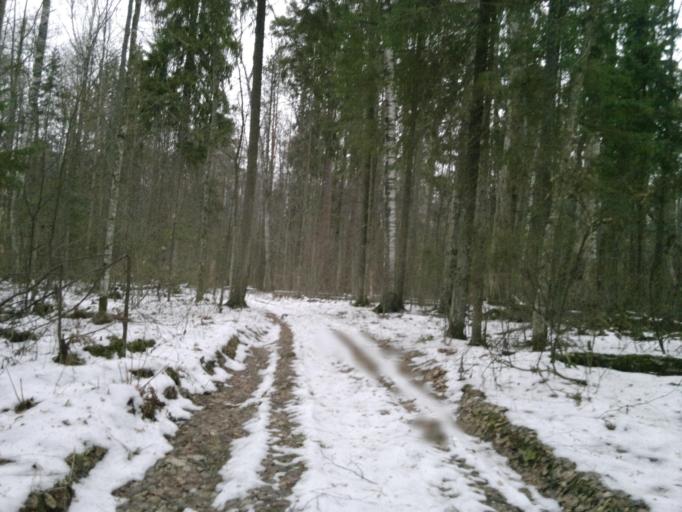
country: RU
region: Mariy-El
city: Yoshkar-Ola
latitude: 56.6058
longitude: 47.9547
